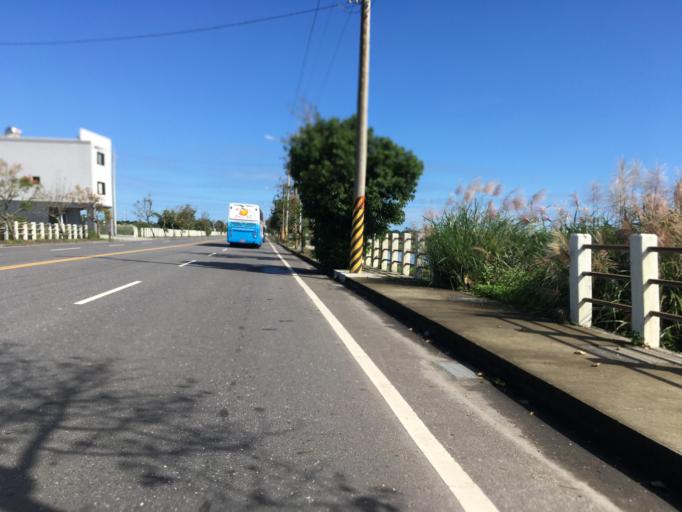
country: TW
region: Taiwan
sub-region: Yilan
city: Yilan
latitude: 24.6153
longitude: 121.8443
